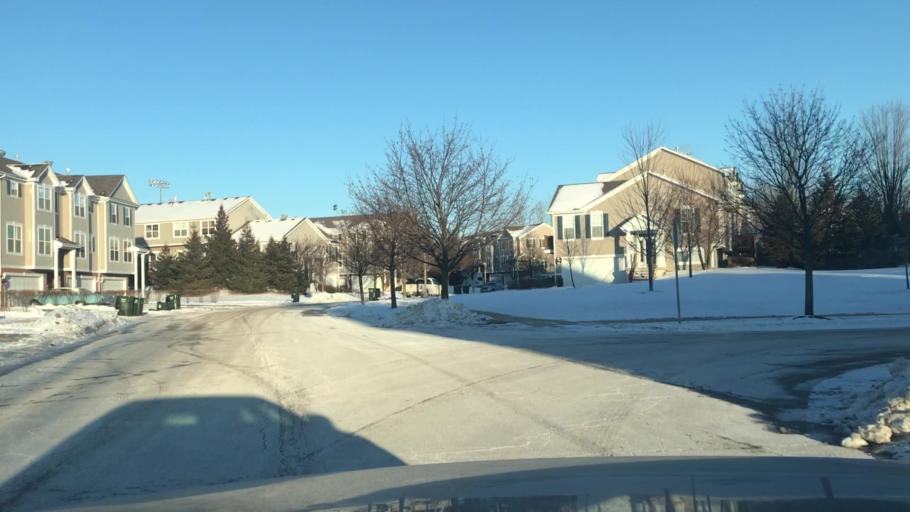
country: US
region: Illinois
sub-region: Kane County
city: Aurora
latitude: 41.7620
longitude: -88.2595
